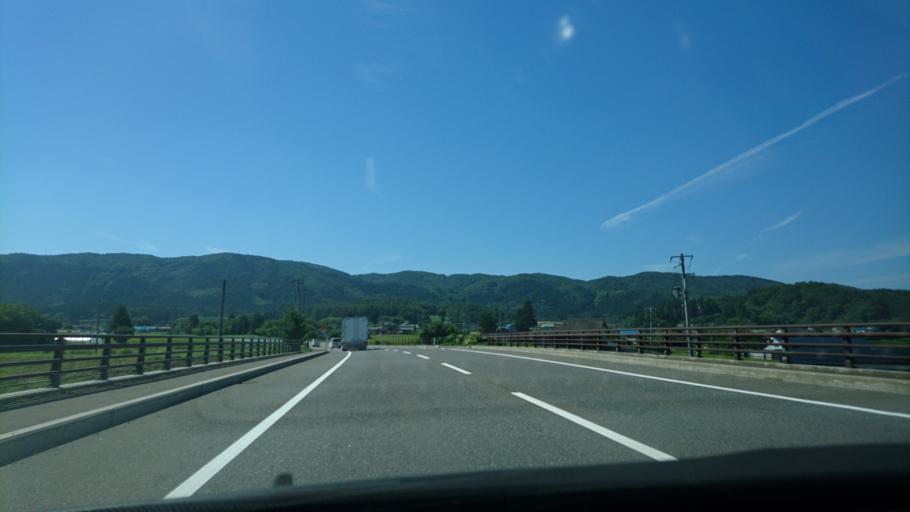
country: JP
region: Iwate
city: Tono
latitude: 39.2826
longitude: 141.5751
